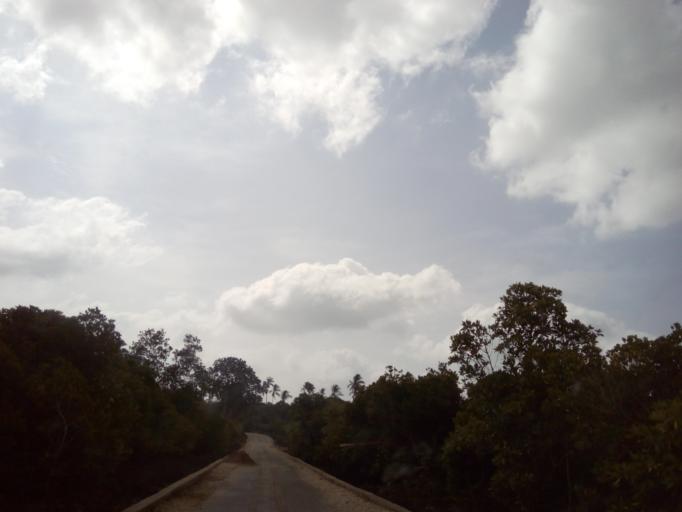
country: TZ
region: Zanzibar Central/South
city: Mahonda
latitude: -6.3238
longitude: 39.3920
